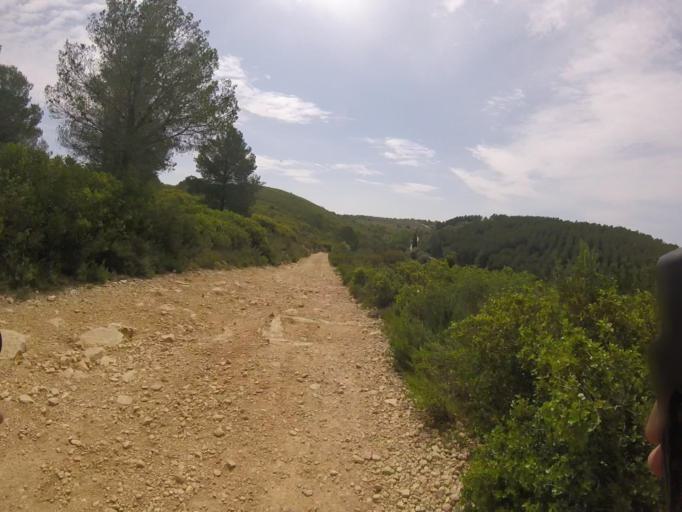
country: ES
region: Valencia
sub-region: Provincia de Castello
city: Cuevas de Vinroma
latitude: 40.2597
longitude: 0.1039
